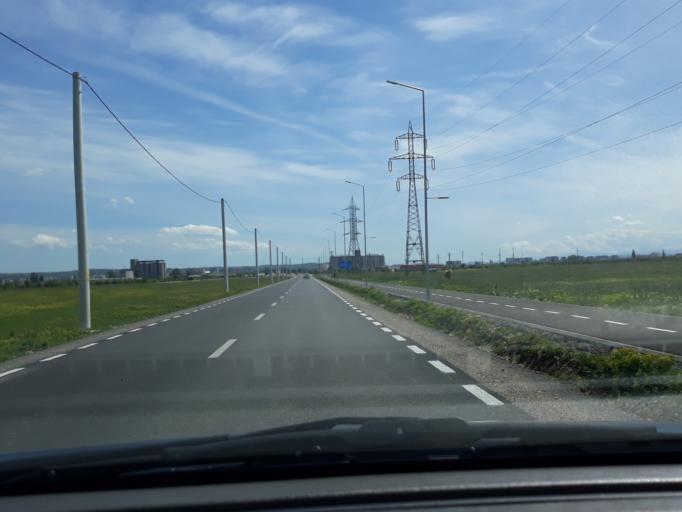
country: RO
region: Bihor
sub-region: Comuna Santandrei
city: Santandrei
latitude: 47.0670
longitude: 21.8722
